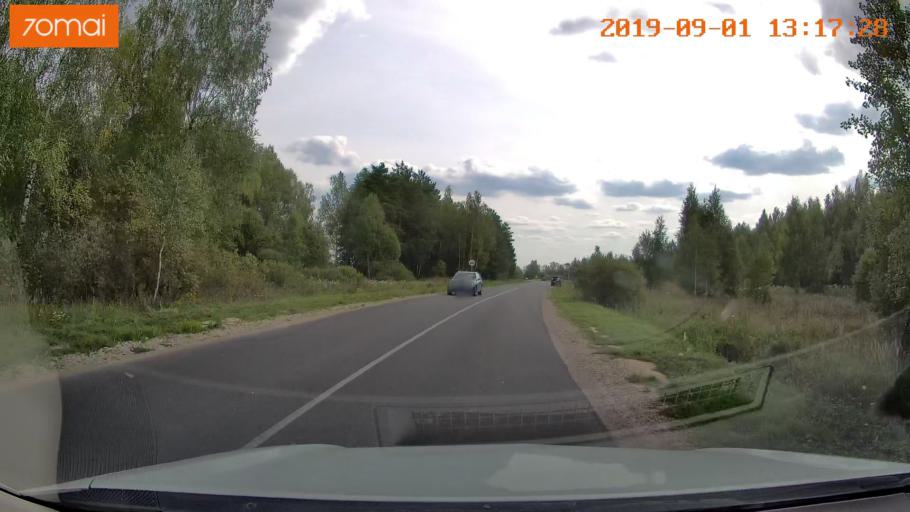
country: RU
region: Kaluga
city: Maloyaroslavets
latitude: 54.9351
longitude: 36.4669
